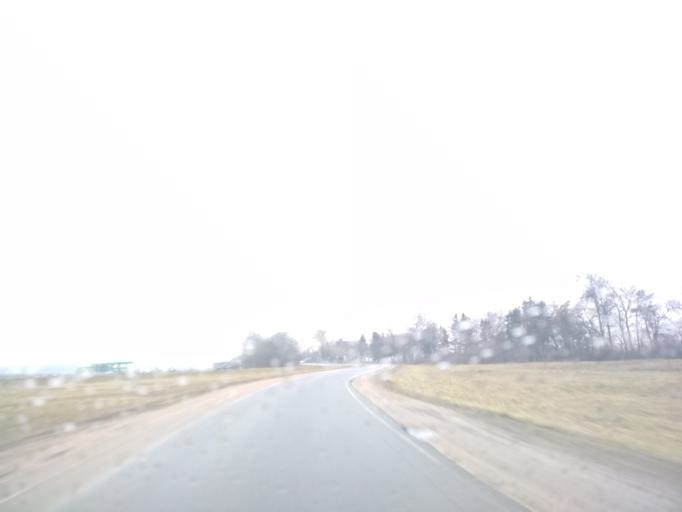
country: BY
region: Minsk
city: Blon'
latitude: 53.5484
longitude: 28.1637
